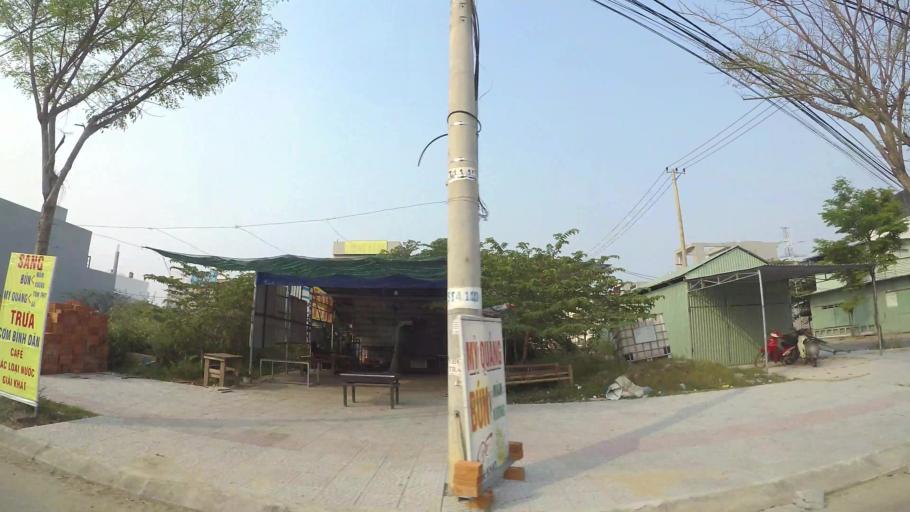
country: VN
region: Da Nang
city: Cam Le
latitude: 16.0081
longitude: 108.2222
